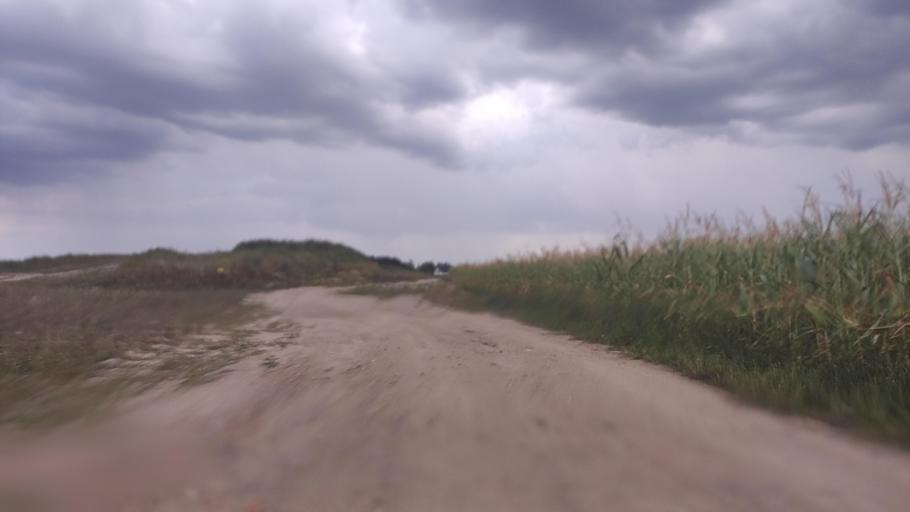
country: PL
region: Greater Poland Voivodeship
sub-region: Powiat poznanski
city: Swarzedz
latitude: 52.3948
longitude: 17.1225
